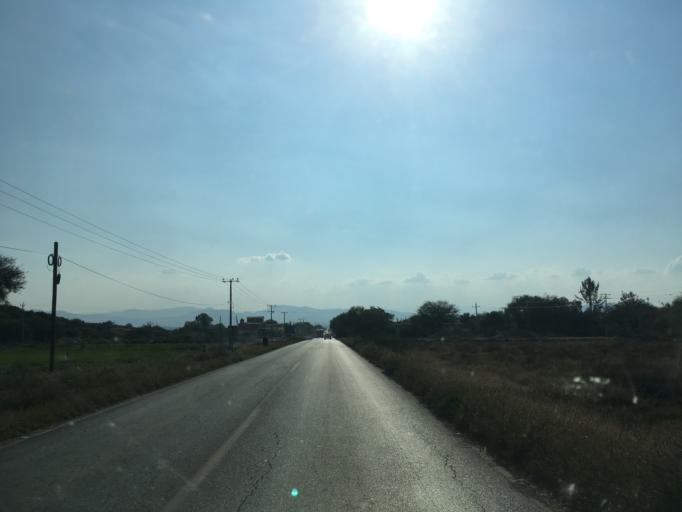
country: MX
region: Hidalgo
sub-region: Ixmiquilpan
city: El Nith
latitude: 20.5539
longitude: -99.1613
